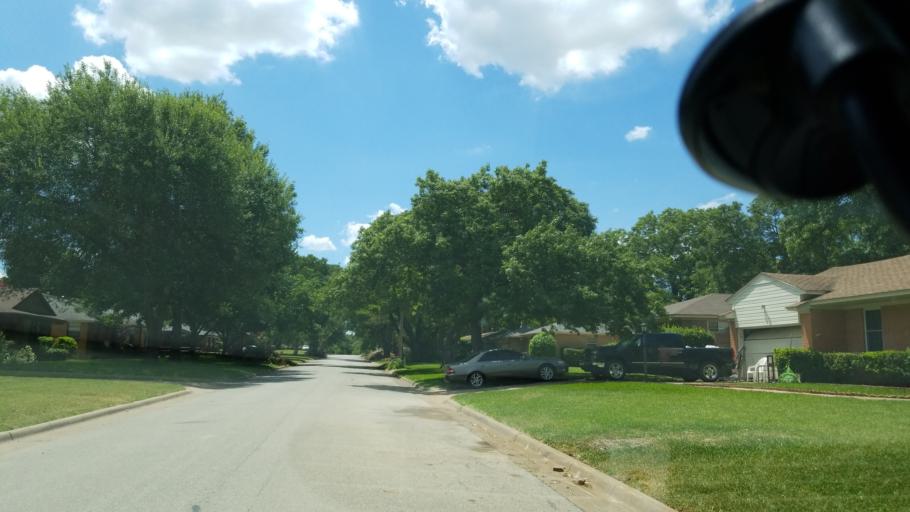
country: US
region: Texas
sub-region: Dallas County
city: Cockrell Hill
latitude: 32.7031
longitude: -96.8648
